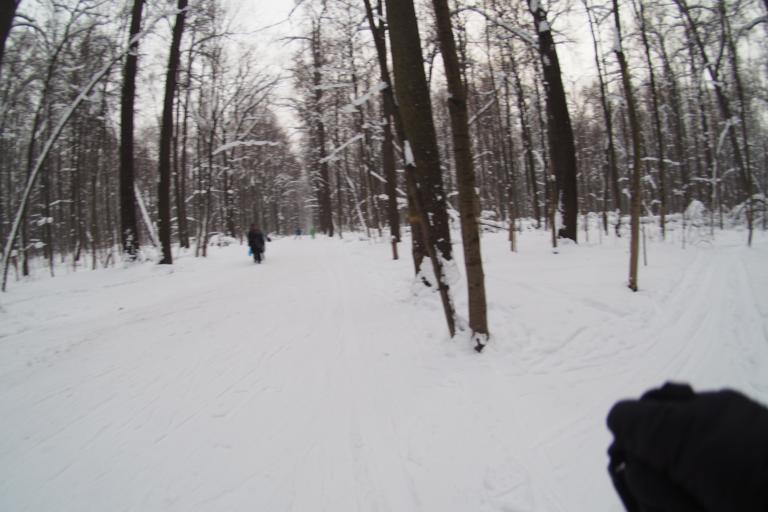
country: RU
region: Moskovskaya
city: Izmaylovo
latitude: 55.7724
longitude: 37.7773
